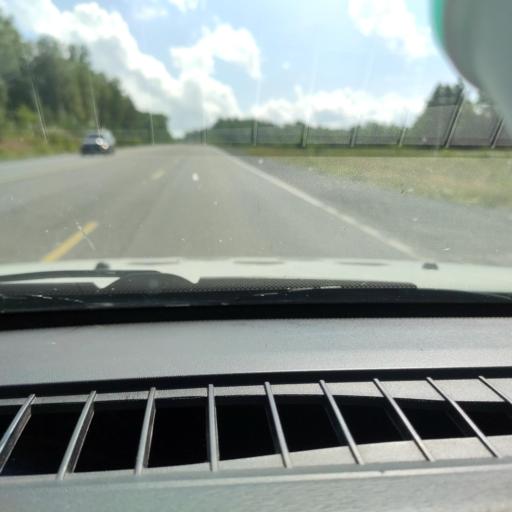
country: RU
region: Chelyabinsk
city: Mezhevoy
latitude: 55.0992
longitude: 58.8765
